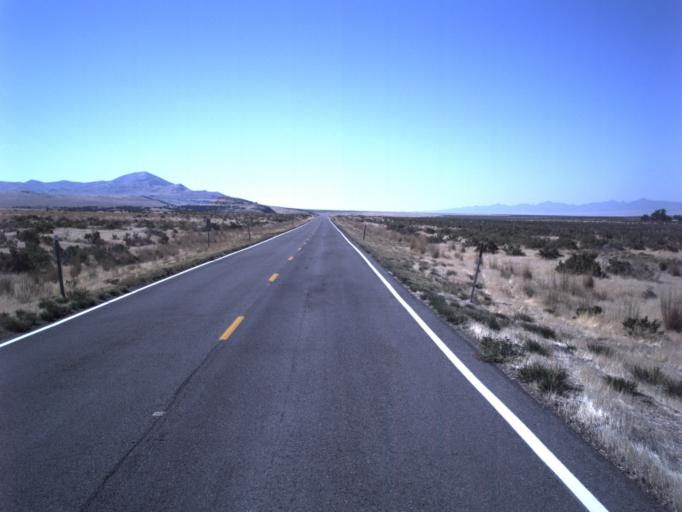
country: US
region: Utah
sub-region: Tooele County
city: Grantsville
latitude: 40.6368
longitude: -112.6919
